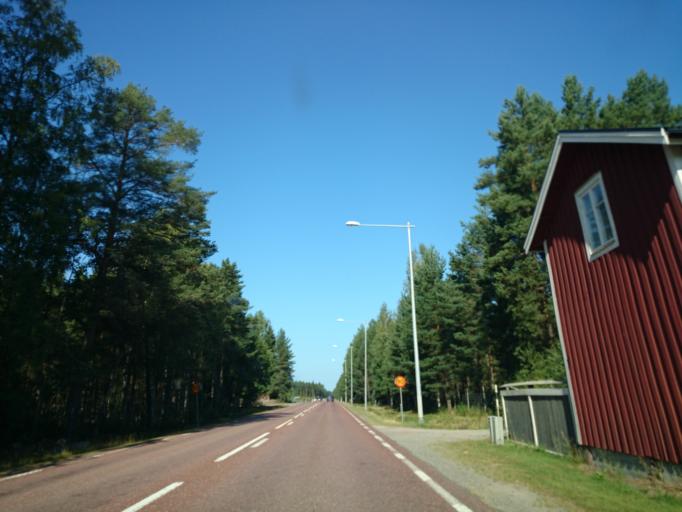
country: SE
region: Gaevleborg
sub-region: Hudiksvalls Kommun
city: Delsbo
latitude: 61.7872
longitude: 16.6093
